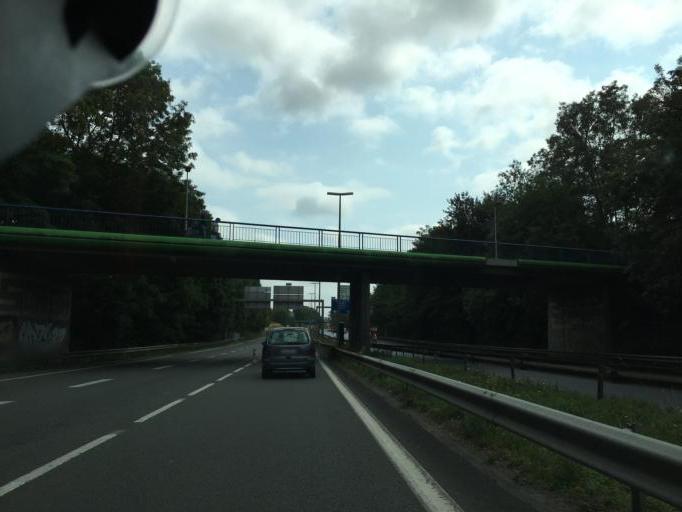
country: FR
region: Nord-Pas-de-Calais
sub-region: Departement du Pas-de-Calais
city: Loison-sous-Lens
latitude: 50.4467
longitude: 2.8389
